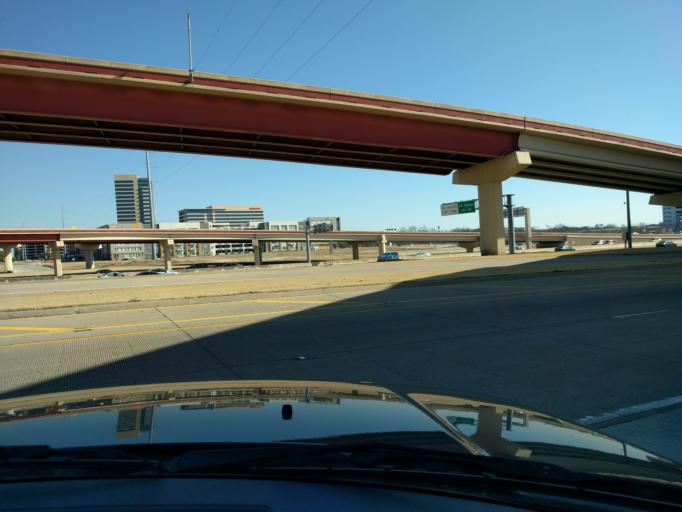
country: US
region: Texas
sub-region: Collin County
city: Plano
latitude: 33.0032
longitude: -96.7092
